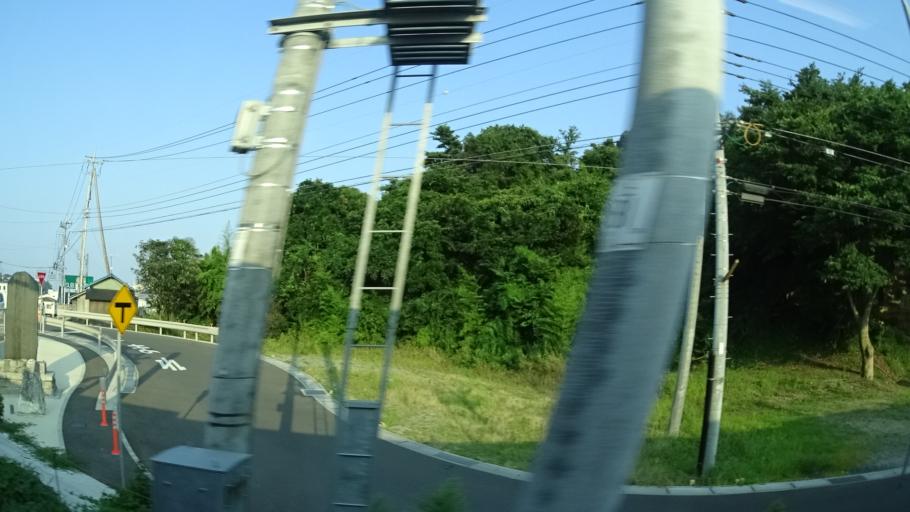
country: JP
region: Ibaraki
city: Funaishikawa
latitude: 36.4944
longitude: 140.6094
